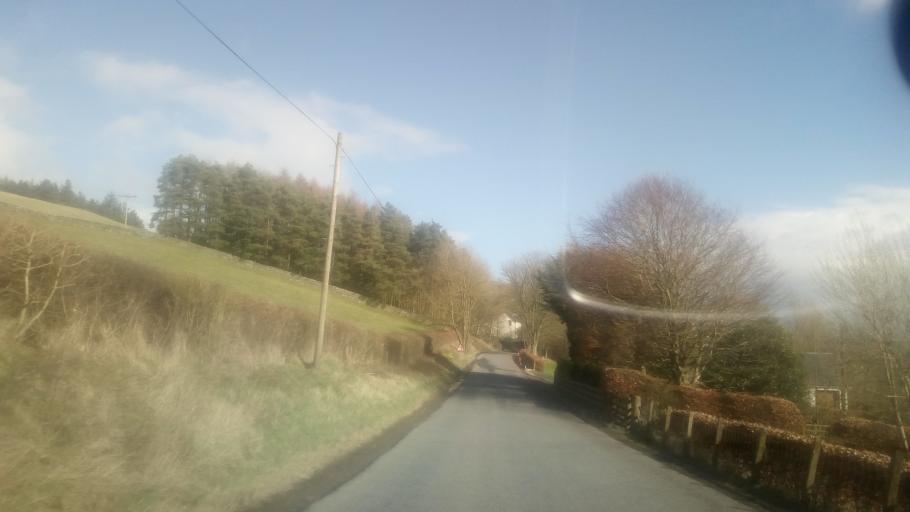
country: GB
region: Scotland
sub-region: The Scottish Borders
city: Hawick
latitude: 55.4176
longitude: -2.8613
